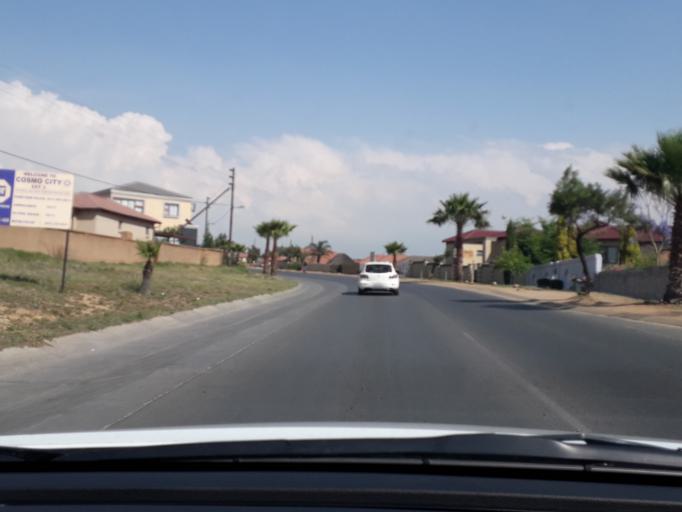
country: ZA
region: Gauteng
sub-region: West Rand District Municipality
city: Muldersdriseloop
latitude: -26.0454
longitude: 27.9229
